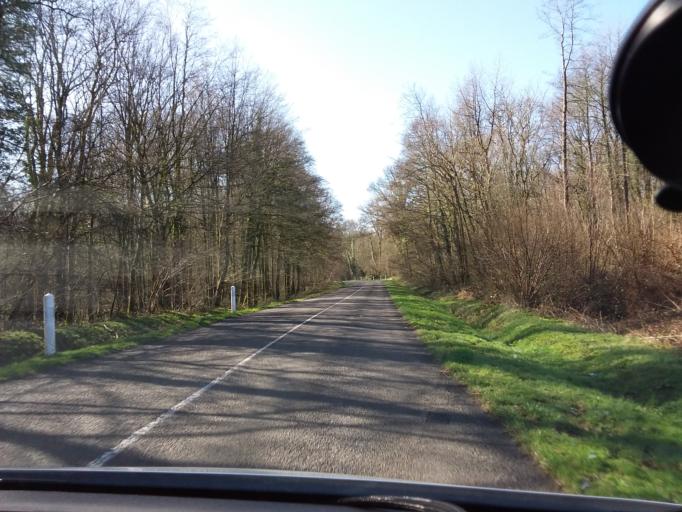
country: FR
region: Picardie
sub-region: Departement de l'Aisne
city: Hirson
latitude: 49.9476
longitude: 4.0772
